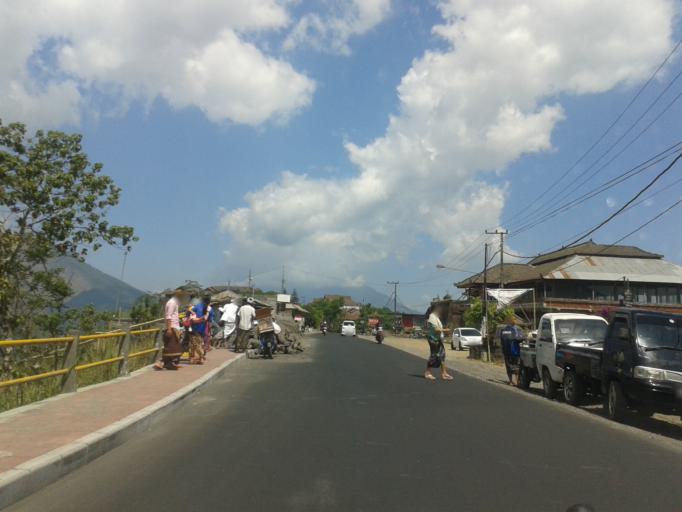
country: ID
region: Bali
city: Banjar Kedisan
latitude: -8.2795
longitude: 115.3569
